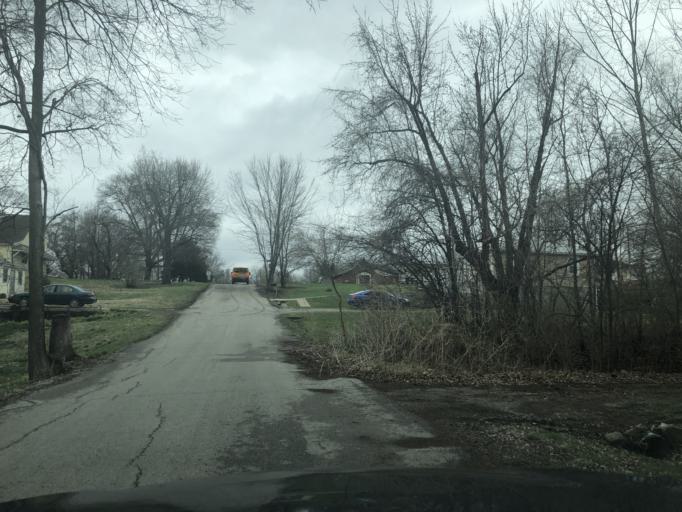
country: US
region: Kansas
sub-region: Leavenworth County
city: Leavenworth
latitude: 39.3027
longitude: -94.9150
